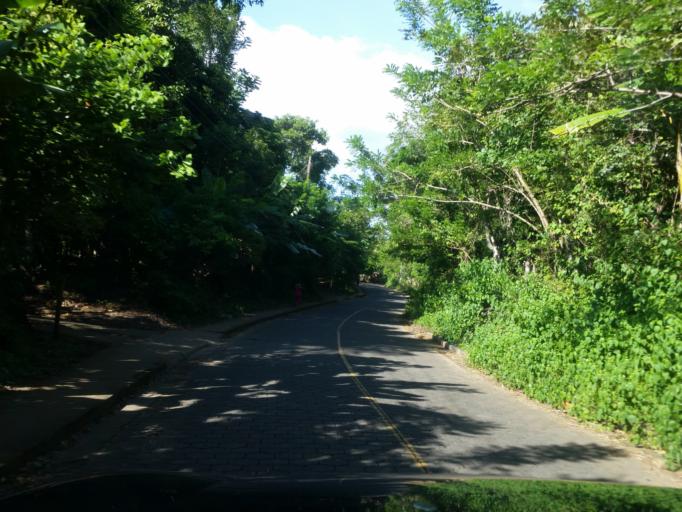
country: NI
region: Masaya
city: Catarina
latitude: 11.9300
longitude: -86.0731
